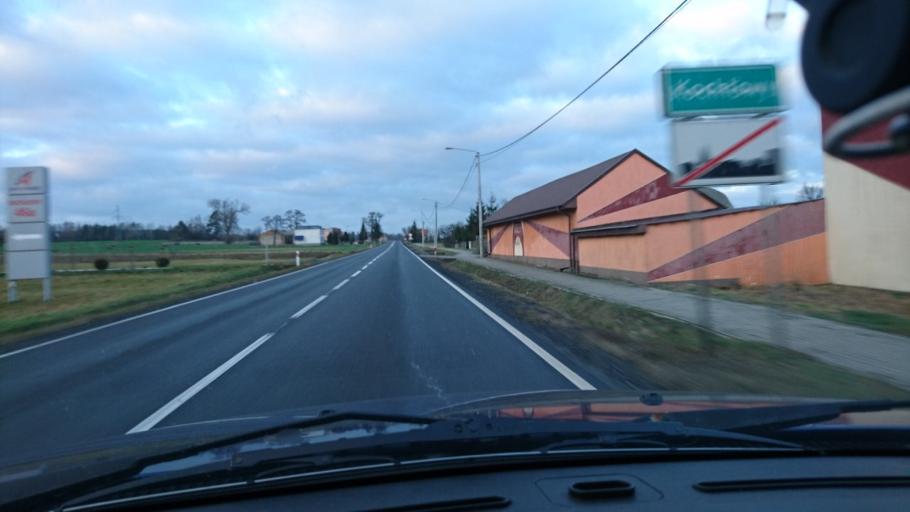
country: PL
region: Greater Poland Voivodeship
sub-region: Powiat ostrzeszowski
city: Ostrzeszow
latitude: 51.3565
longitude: 17.9470
